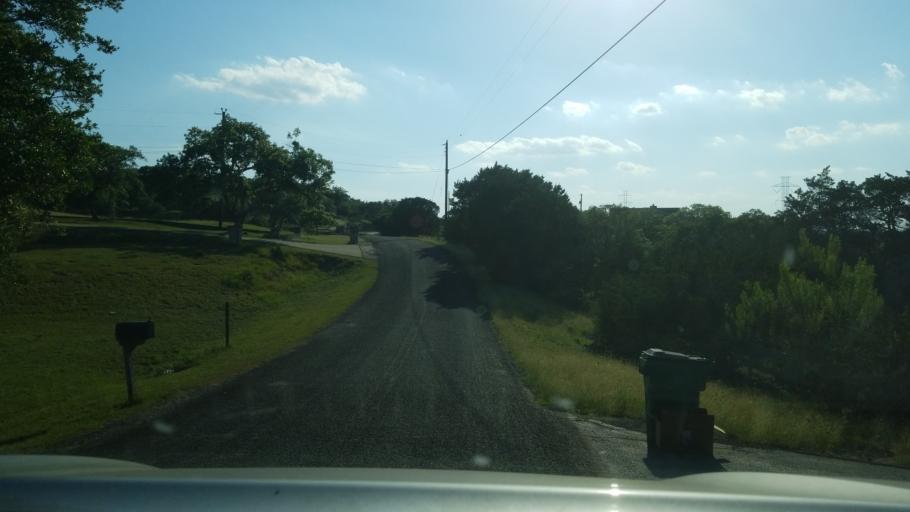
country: US
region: Texas
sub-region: Comal County
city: Bulverde
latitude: 29.7828
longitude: -98.4434
